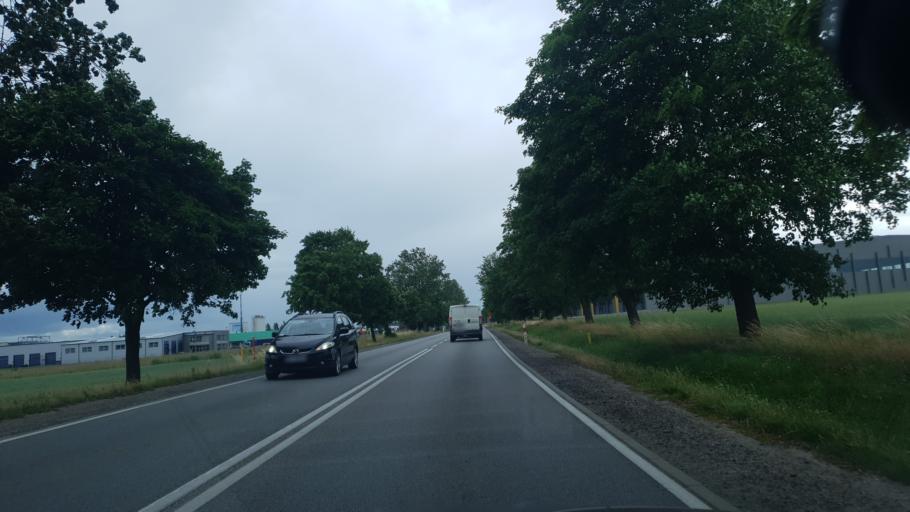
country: PL
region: Pomeranian Voivodeship
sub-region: Powiat kartuski
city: Chwaszczyno
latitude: 54.4248
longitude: 18.3852
